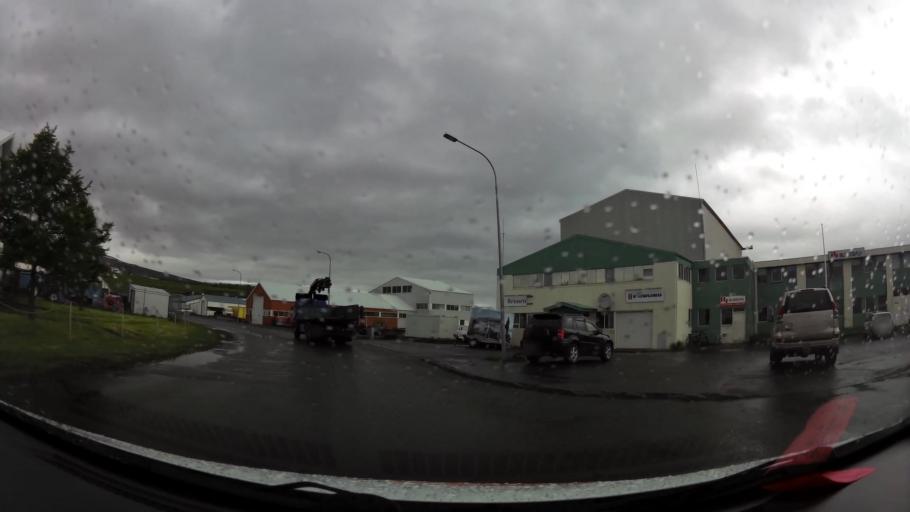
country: IS
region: Northeast
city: Akureyri
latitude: 65.6943
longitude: -18.1013
